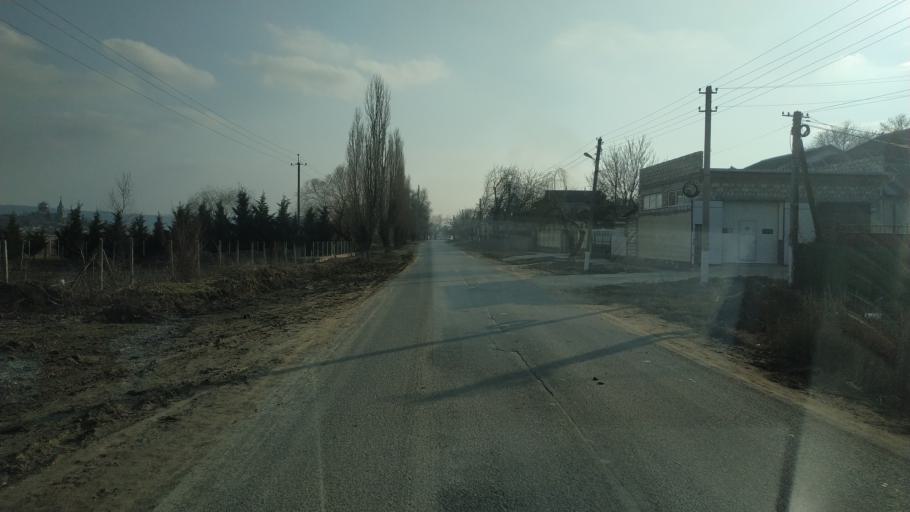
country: MD
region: Hincesti
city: Dancu
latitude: 46.7810
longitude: 28.3488
